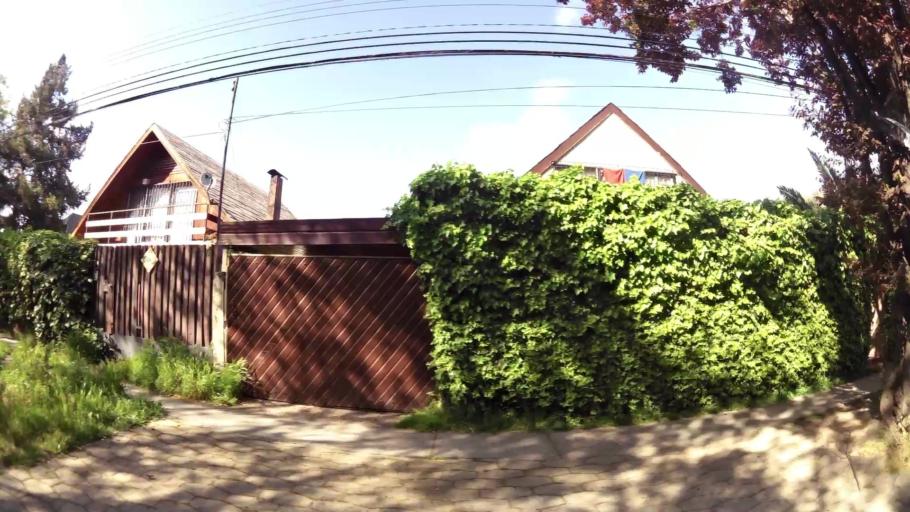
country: CL
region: Santiago Metropolitan
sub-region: Provincia de Santiago
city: Villa Presidente Frei, Nunoa, Santiago, Chile
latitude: -33.4416
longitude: -70.5554
